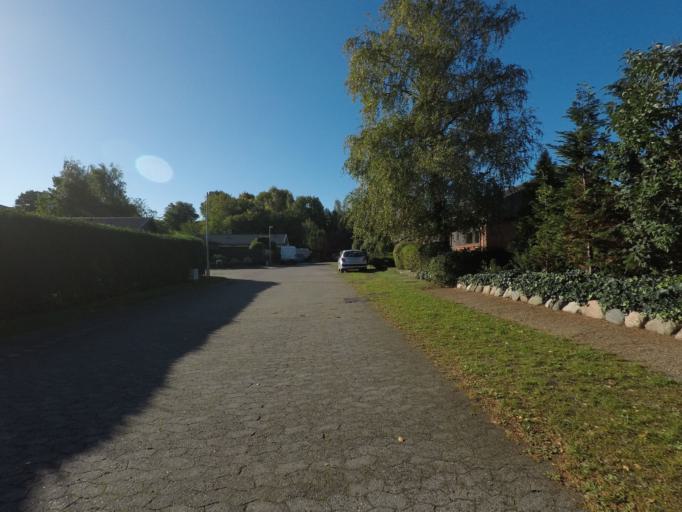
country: DK
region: Capital Region
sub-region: Ballerup Kommune
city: Malov
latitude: 55.7568
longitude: 12.3263
